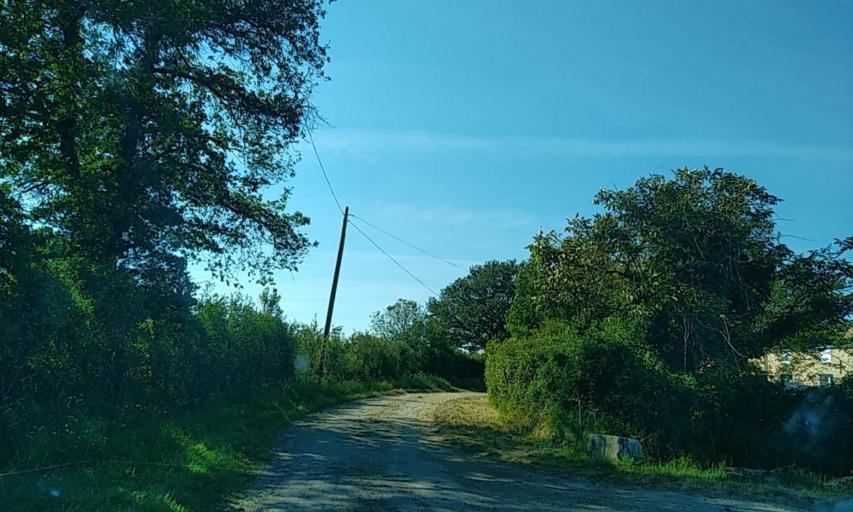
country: FR
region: Poitou-Charentes
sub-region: Departement des Deux-Sevres
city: Boisme
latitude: 46.8054
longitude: -0.4132
